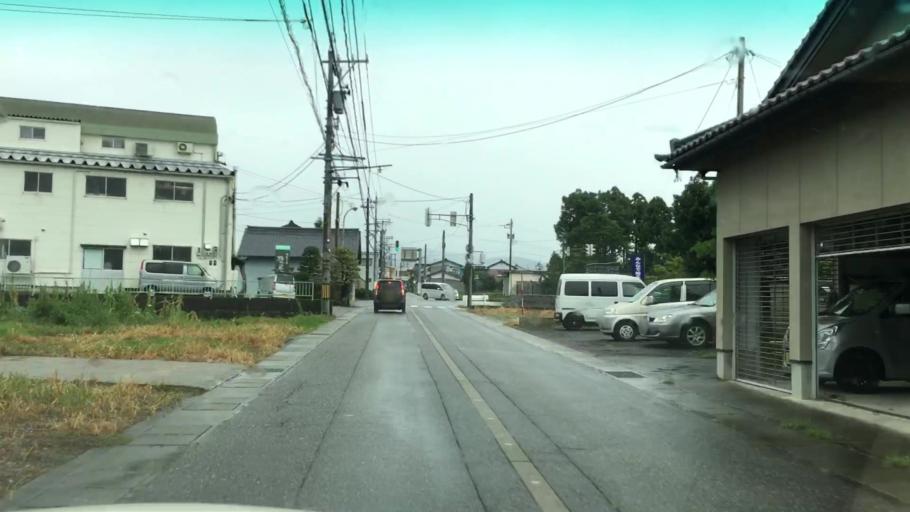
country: JP
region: Toyama
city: Kamiichi
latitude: 36.6516
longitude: 137.3193
